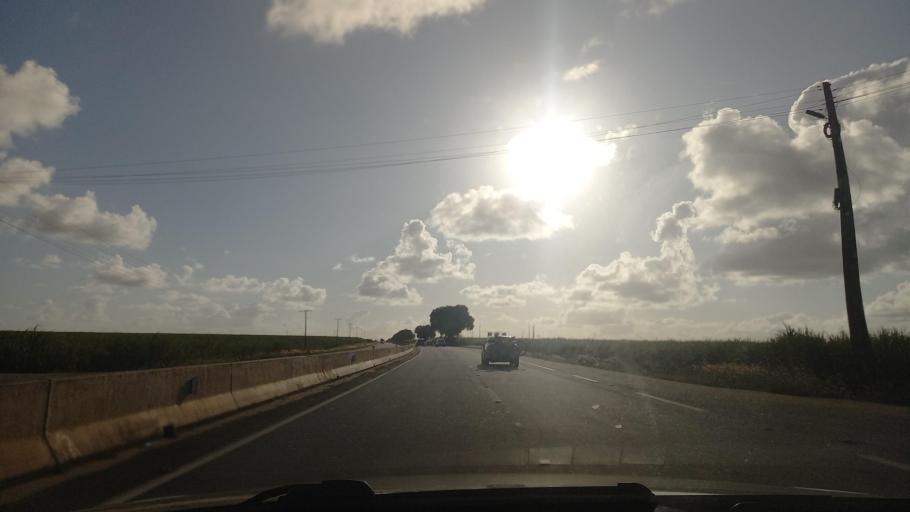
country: BR
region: Alagoas
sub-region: Sao Miguel Dos Campos
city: Sao Miguel dos Campos
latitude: -9.8060
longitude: -36.1219
